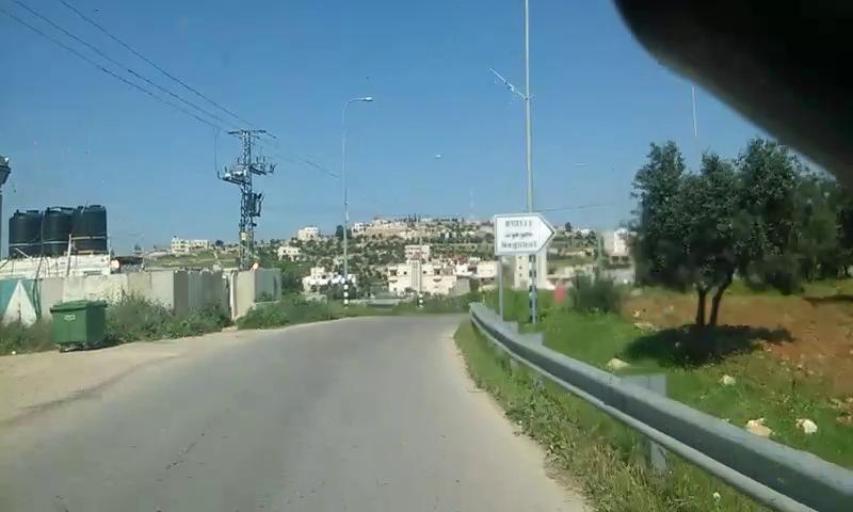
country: PS
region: West Bank
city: Bayt `Awwa
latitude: 31.4990
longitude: 34.9618
